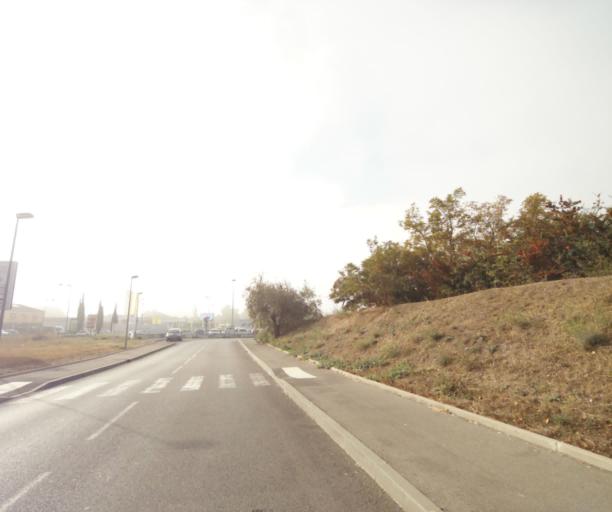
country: FR
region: Provence-Alpes-Cote d'Azur
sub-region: Departement des Bouches-du-Rhone
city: Saint-Victoret
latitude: 43.4197
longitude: 5.2286
